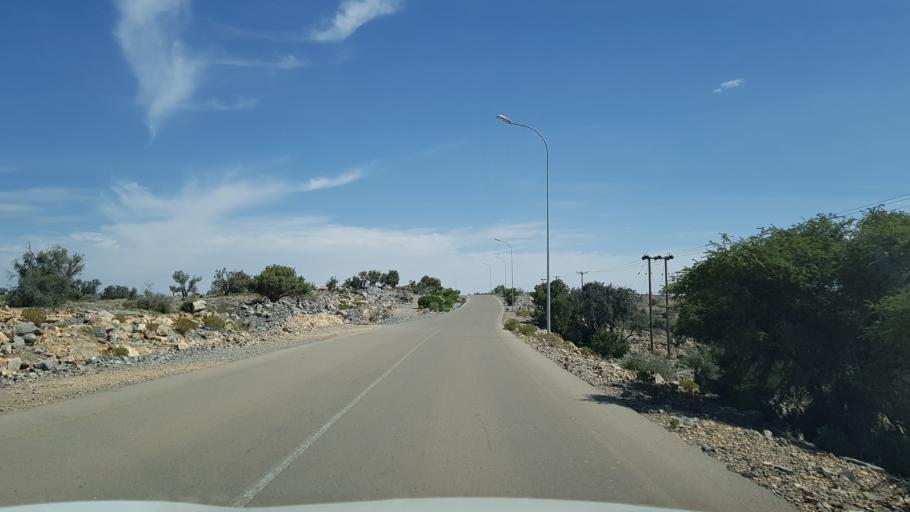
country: OM
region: Al Batinah
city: Bayt al `Awabi
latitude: 23.1275
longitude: 57.5988
